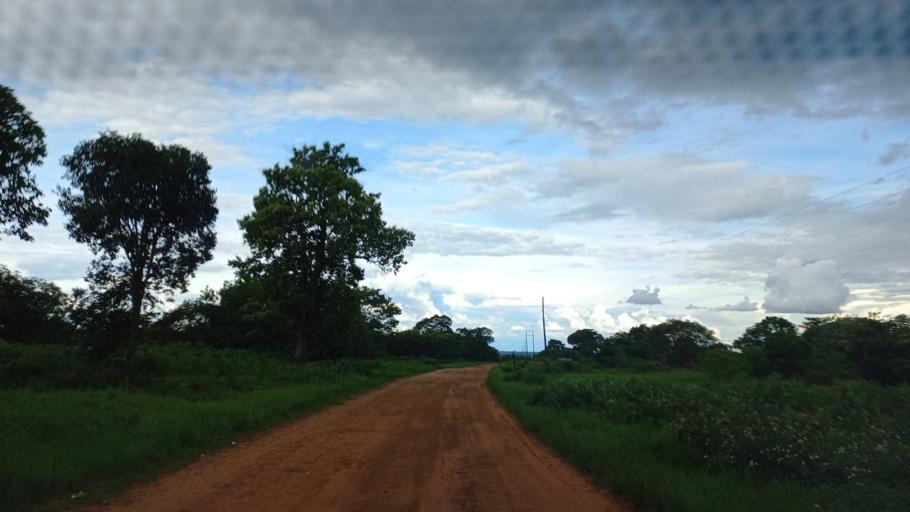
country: ZM
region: North-Western
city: Mwinilunga
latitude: -11.7761
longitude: 24.3868
